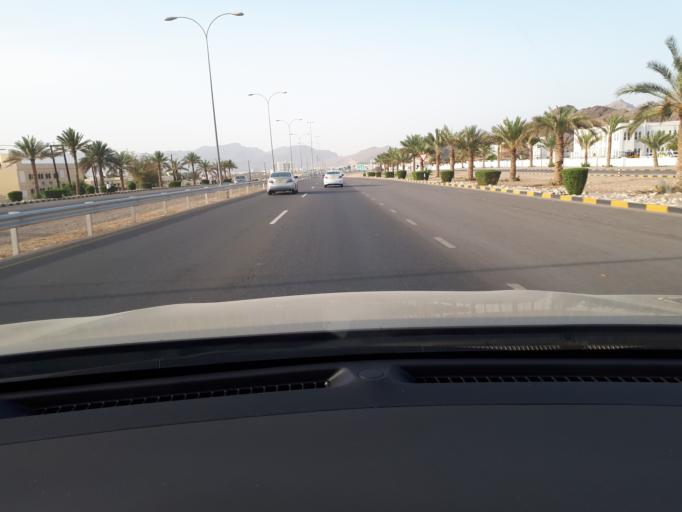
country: OM
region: Muhafazat Masqat
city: Bawshar
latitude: 23.4726
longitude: 58.4951
